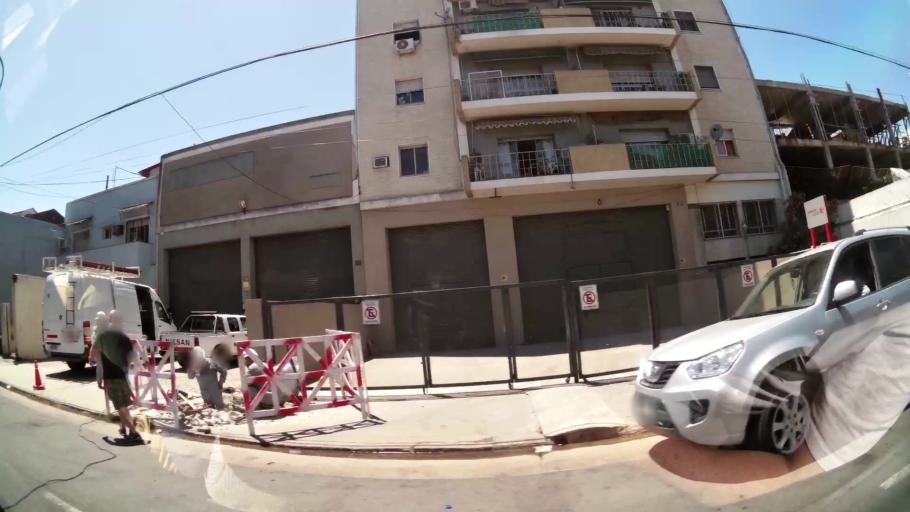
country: AR
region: Buenos Aires
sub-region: Partido de Avellaneda
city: Avellaneda
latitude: -34.6447
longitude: -58.3790
